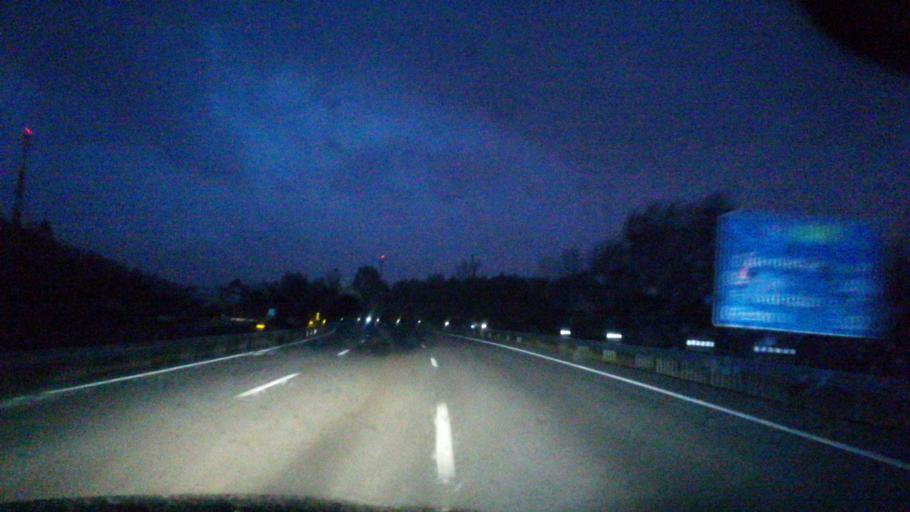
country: PT
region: Braga
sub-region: Vizela
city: Vizela
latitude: 41.4054
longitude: -8.2701
